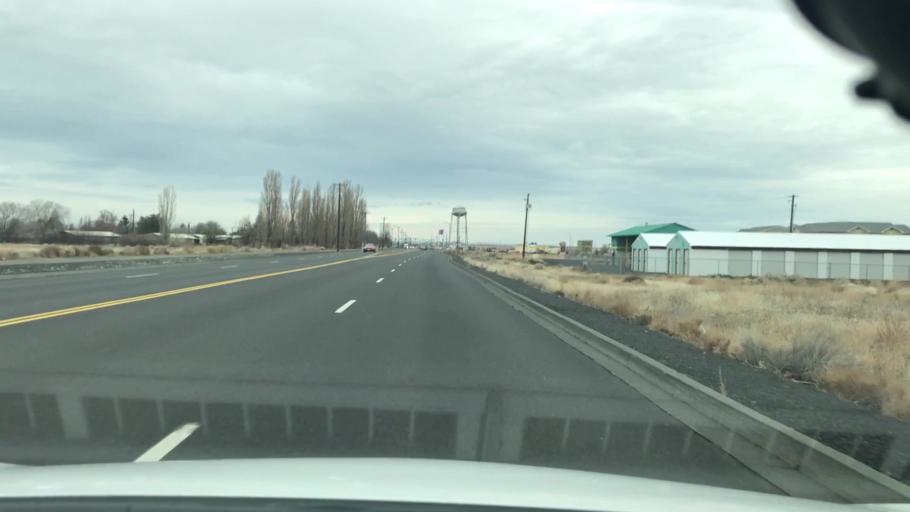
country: US
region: Washington
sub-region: Grant County
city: Cascade Valley
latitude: 47.1589
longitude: -119.3115
